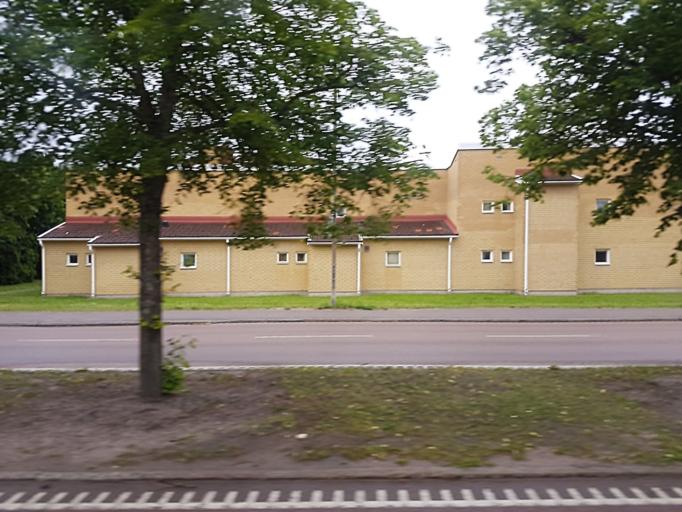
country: SE
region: Uppsala
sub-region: Uppsala Kommun
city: Uppsala
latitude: 59.8701
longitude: 17.6638
